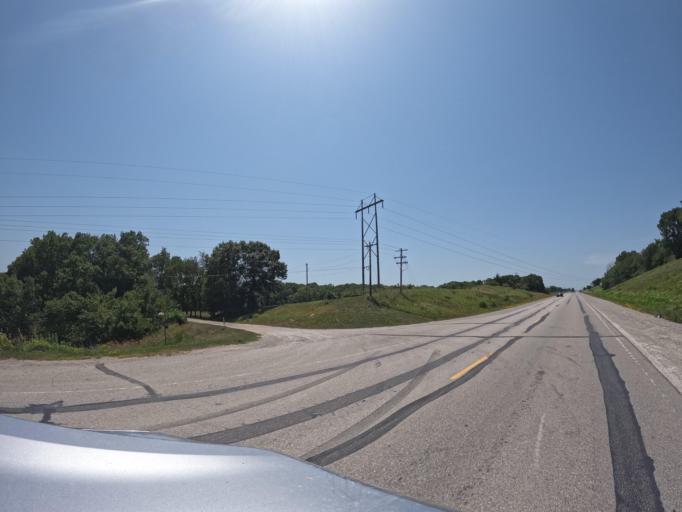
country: US
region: Iowa
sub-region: Henry County
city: Mount Pleasant
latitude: 40.9673
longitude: -91.6043
